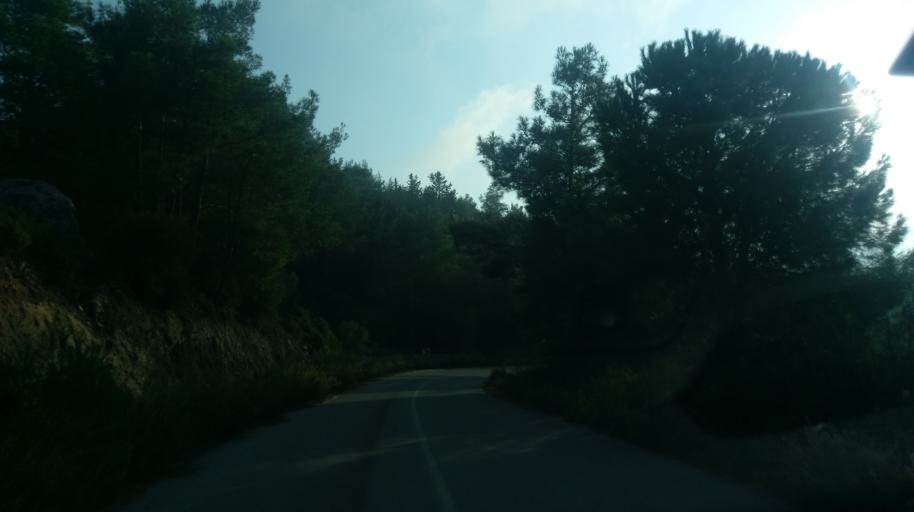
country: CY
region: Ammochostos
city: Trikomo
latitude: 35.3799
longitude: 33.8635
